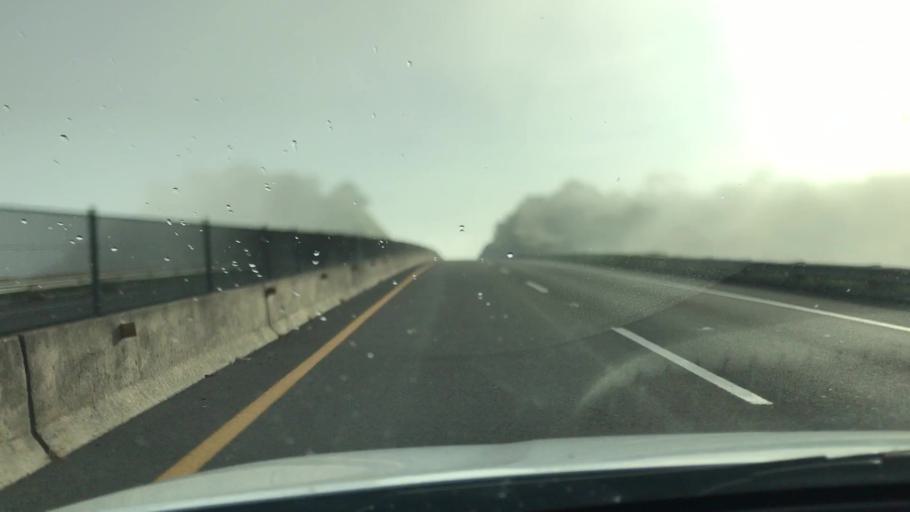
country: MX
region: Jalisco
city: Jalostotitlan
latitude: 21.1519
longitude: -102.4234
